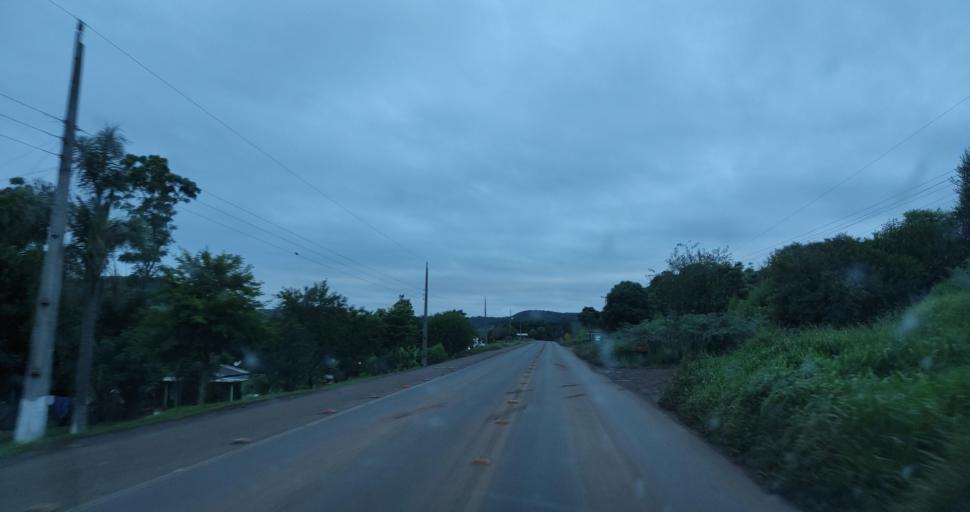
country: BR
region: Santa Catarina
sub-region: Xanxere
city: Xanxere
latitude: -26.6673
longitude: -52.4350
